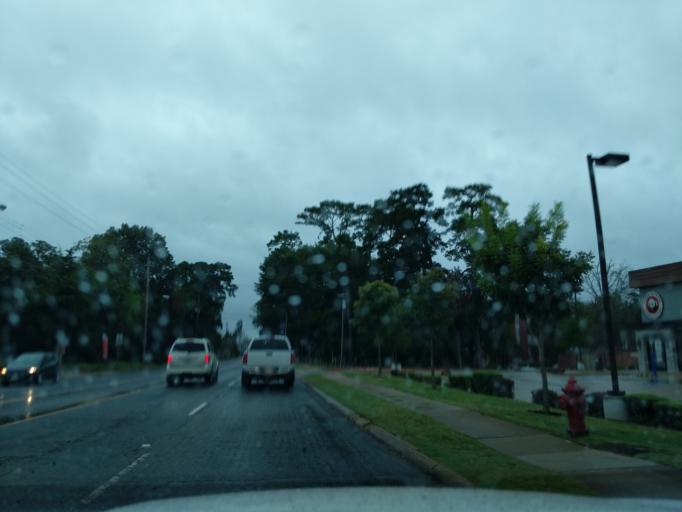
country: US
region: Texas
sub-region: Nacogdoches County
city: Nacogdoches
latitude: 31.6169
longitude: -94.6527
